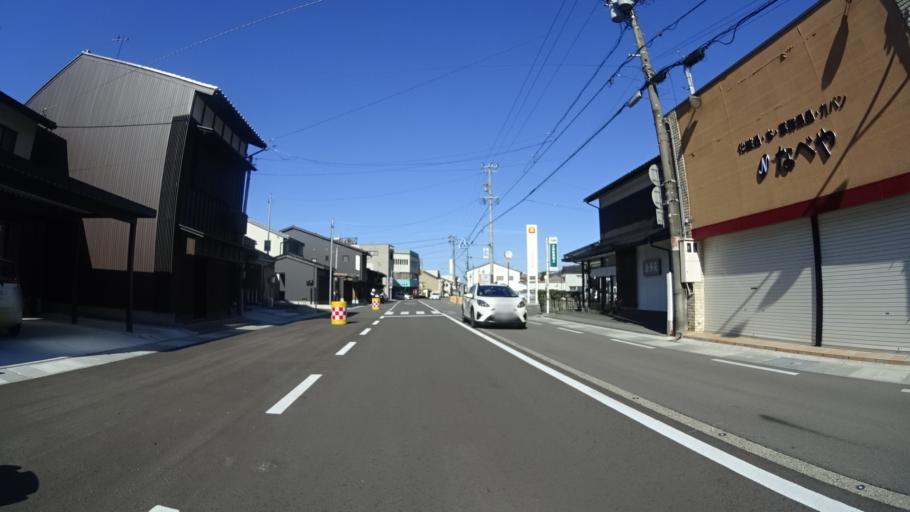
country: JP
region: Ishikawa
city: Tsurugi-asahimachi
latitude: 36.4469
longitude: 136.6275
